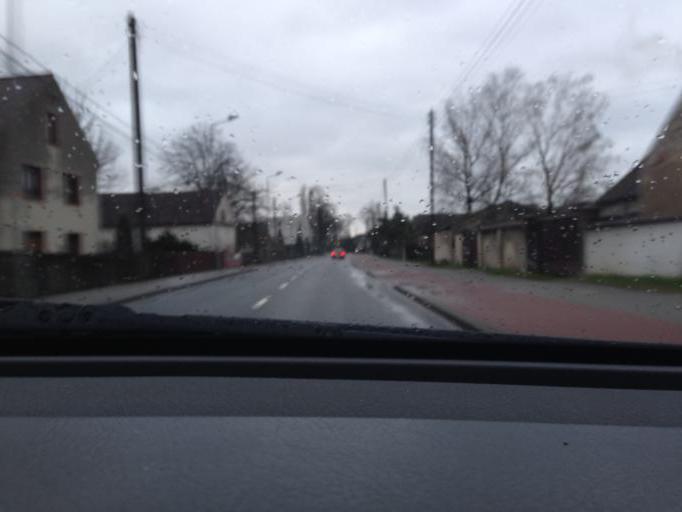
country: PL
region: Opole Voivodeship
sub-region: Powiat opolski
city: Opole
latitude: 50.6884
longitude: 17.9521
